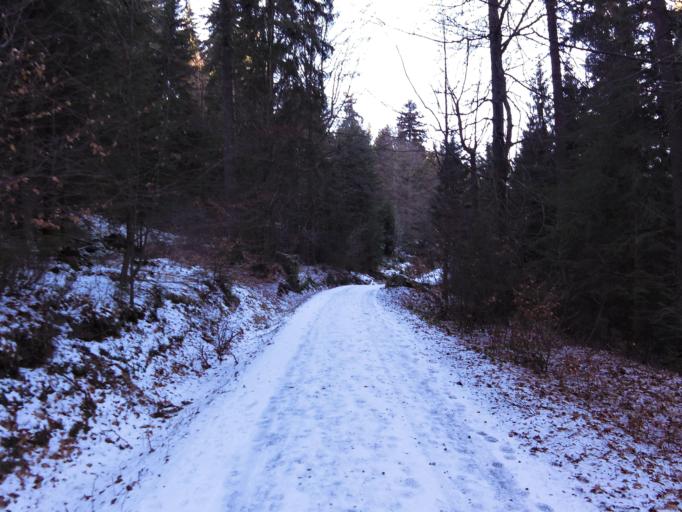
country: DE
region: Bavaria
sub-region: Upper Franconia
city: Fichtelberg
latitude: 50.0370
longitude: 11.8311
